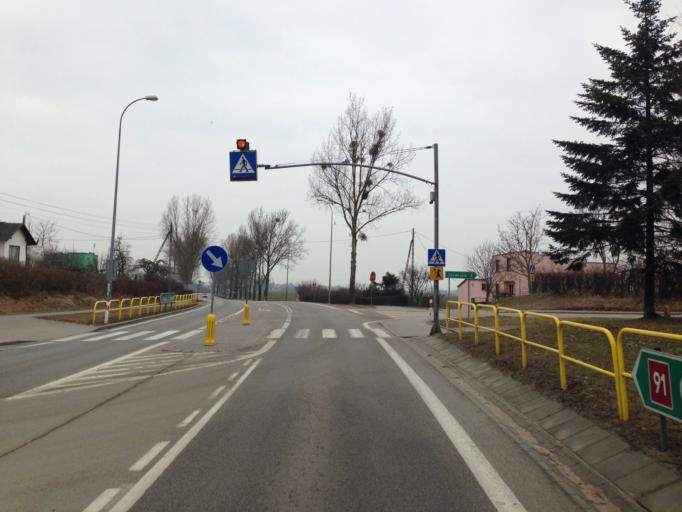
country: PL
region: Pomeranian Voivodeship
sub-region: Powiat starogardzki
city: Smetowo Graniczne
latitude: 53.7665
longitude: 18.7678
